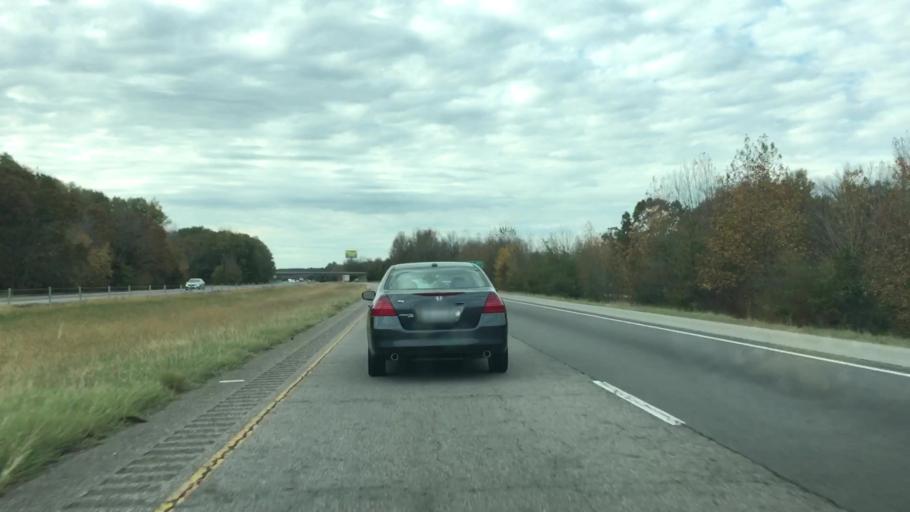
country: US
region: Arkansas
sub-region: Faulkner County
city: Conway
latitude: 35.1513
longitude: -92.5475
